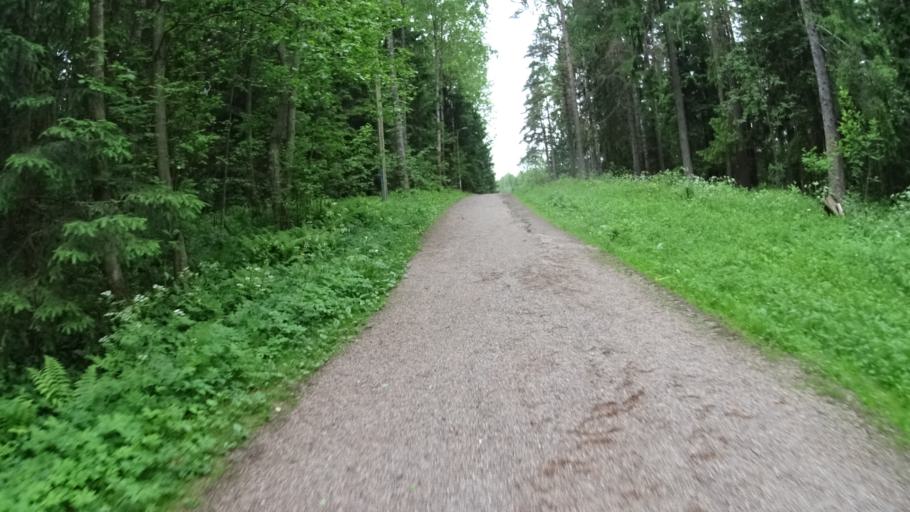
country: FI
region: Uusimaa
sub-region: Helsinki
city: Kilo
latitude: 60.2738
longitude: 24.8273
